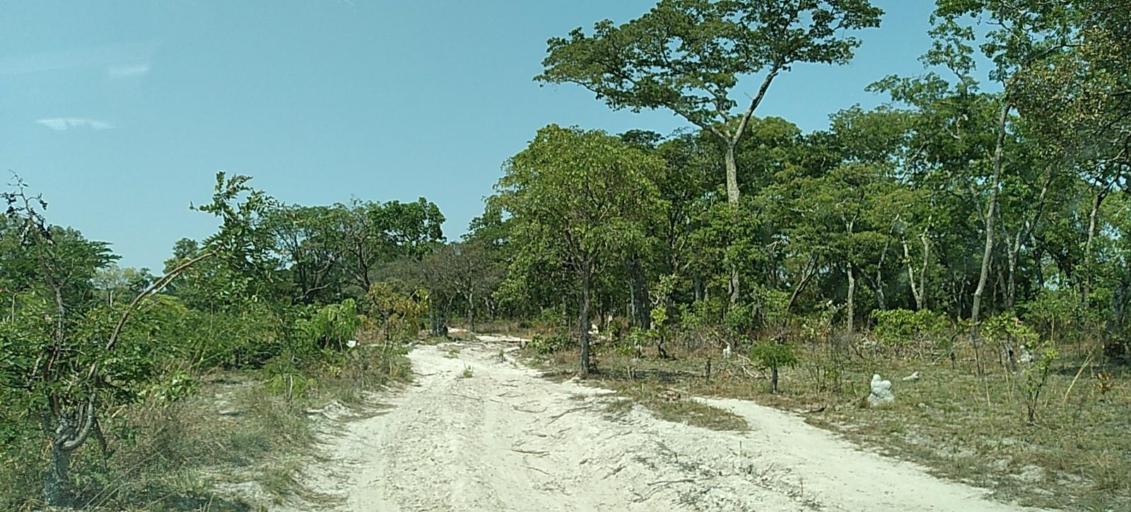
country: ZM
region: Copperbelt
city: Mpongwe
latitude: -13.7807
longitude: 28.1060
